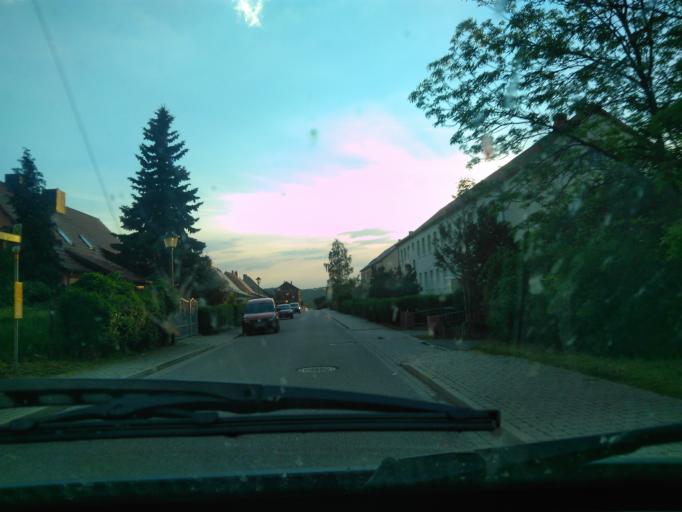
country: DE
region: Saxony-Anhalt
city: Wethau
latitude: 51.1215
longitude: 11.8797
